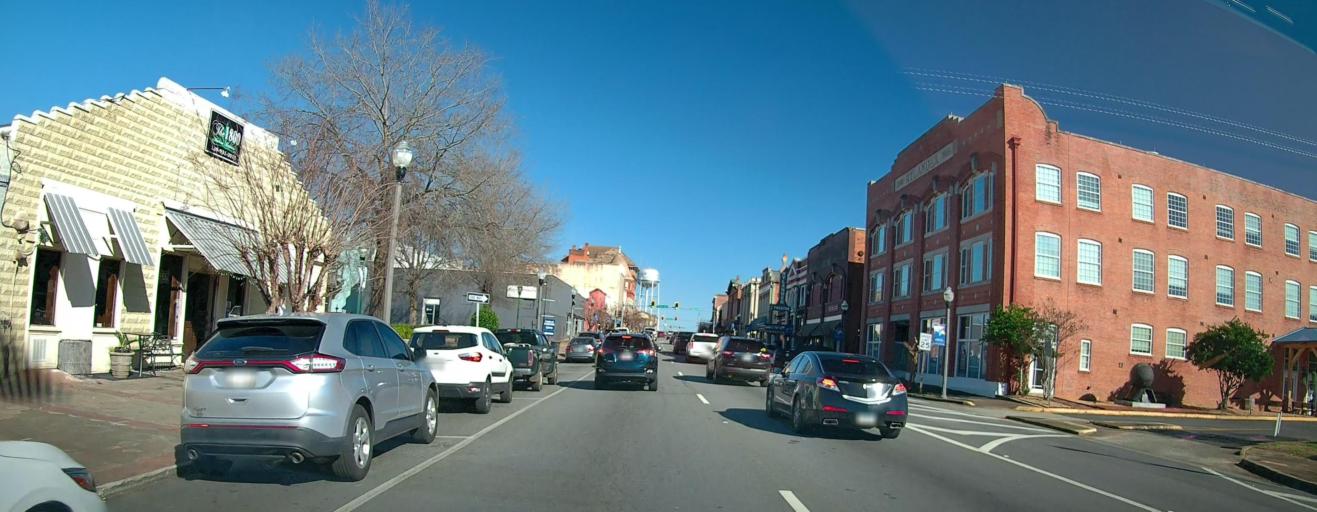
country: US
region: Georgia
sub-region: Sumter County
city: Americus
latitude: 32.0722
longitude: -84.2362
